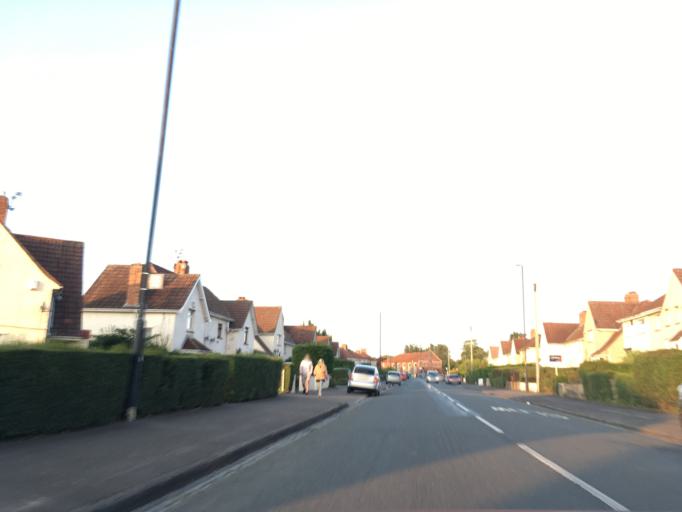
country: GB
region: England
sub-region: South Gloucestershire
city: Kingswood
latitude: 51.4690
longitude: -2.5321
